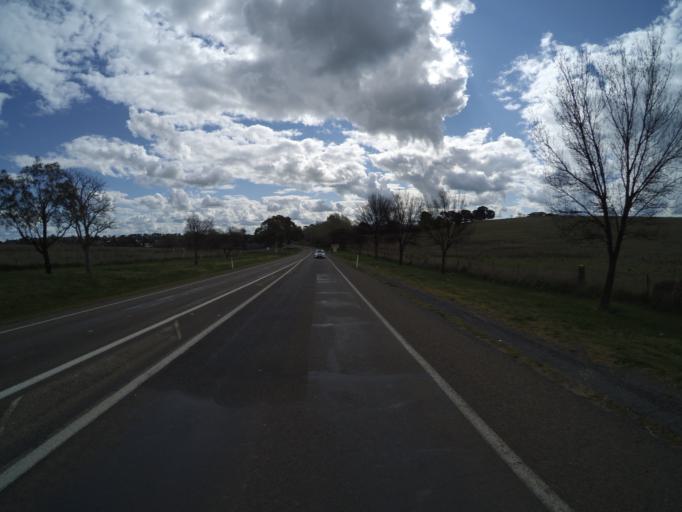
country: AU
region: New South Wales
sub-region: Yass Valley
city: Yass
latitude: -34.8525
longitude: 148.9256
